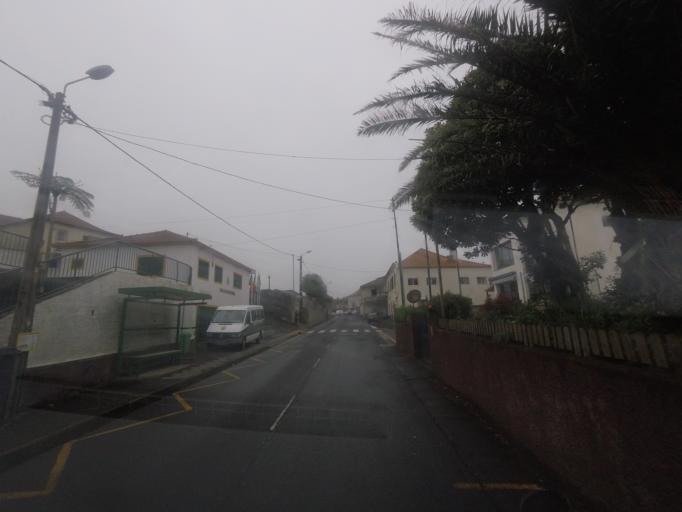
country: PT
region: Madeira
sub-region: Santa Cruz
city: Santa Cruz
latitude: 32.7247
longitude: -16.8203
